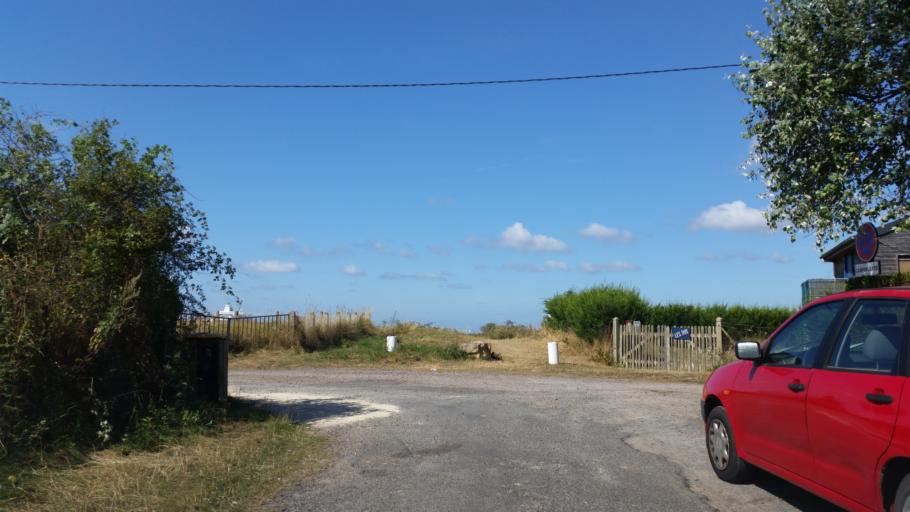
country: FR
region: Lower Normandy
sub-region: Departement du Calvados
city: Ouistreham
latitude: 49.2787
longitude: -0.2463
